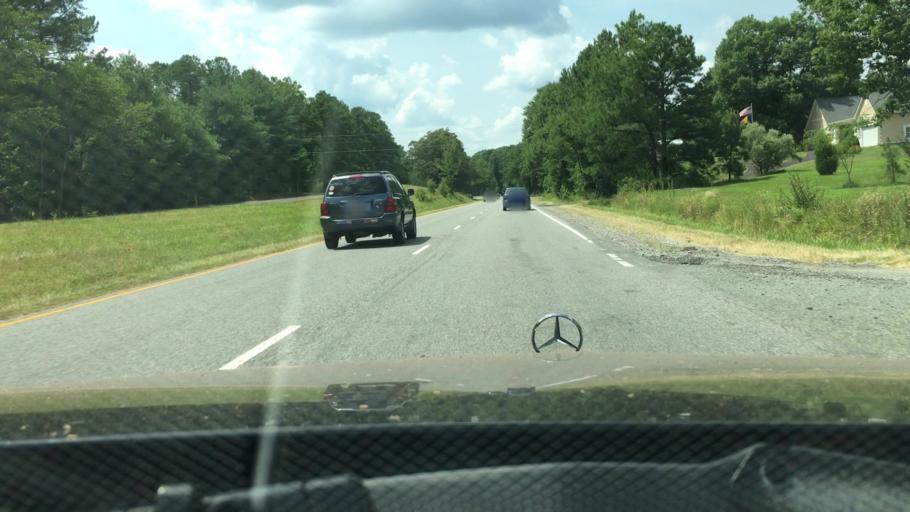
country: US
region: Virginia
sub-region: Spotsylvania County
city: Spotsylvania
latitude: 38.3168
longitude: -77.6876
